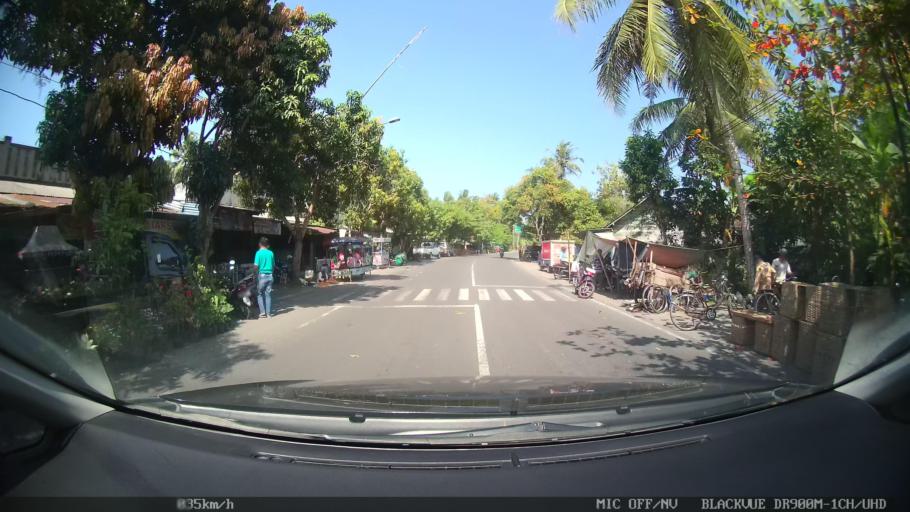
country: ID
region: Daerah Istimewa Yogyakarta
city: Srandakan
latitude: -7.9493
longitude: 110.2208
